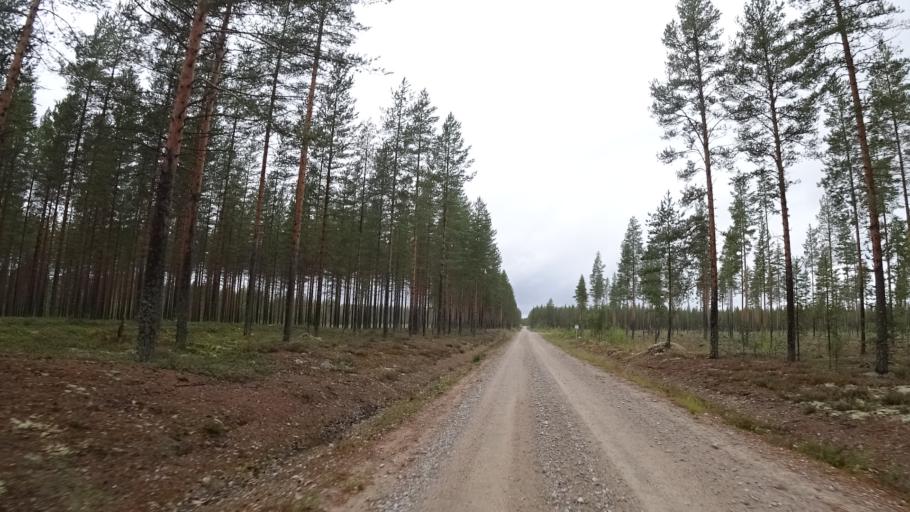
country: FI
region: North Karelia
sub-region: Pielisen Karjala
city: Lieksa
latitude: 63.5262
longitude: 30.0861
